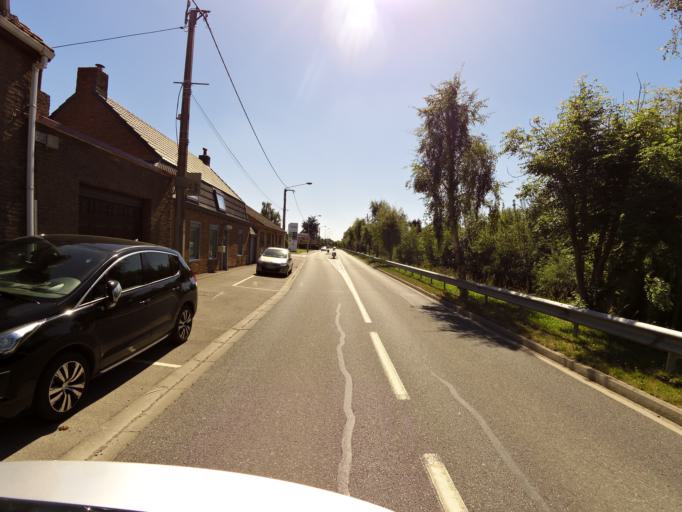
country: FR
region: Nord-Pas-de-Calais
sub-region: Departement du Nord
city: Hoymille
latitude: 50.9769
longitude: 2.4457
